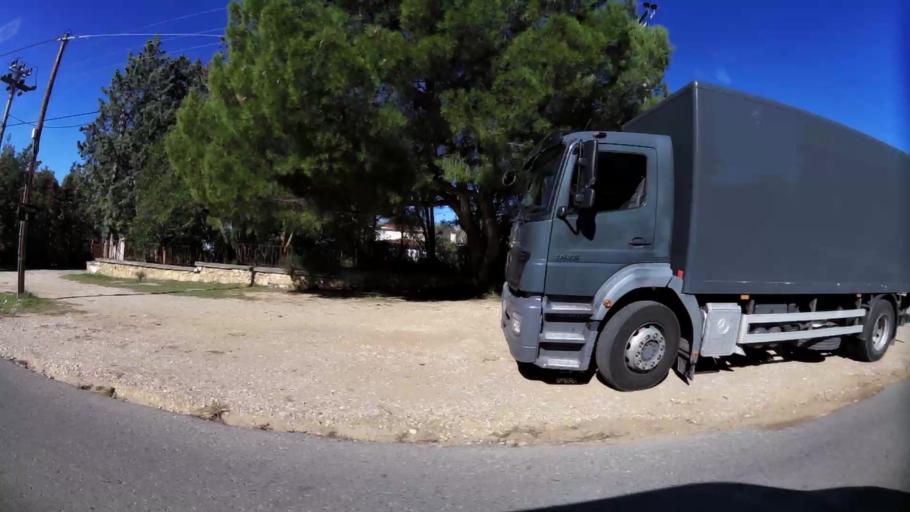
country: GR
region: Attica
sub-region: Nomarchia Anatolikis Attikis
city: Varybobi
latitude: 38.1243
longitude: 23.7933
